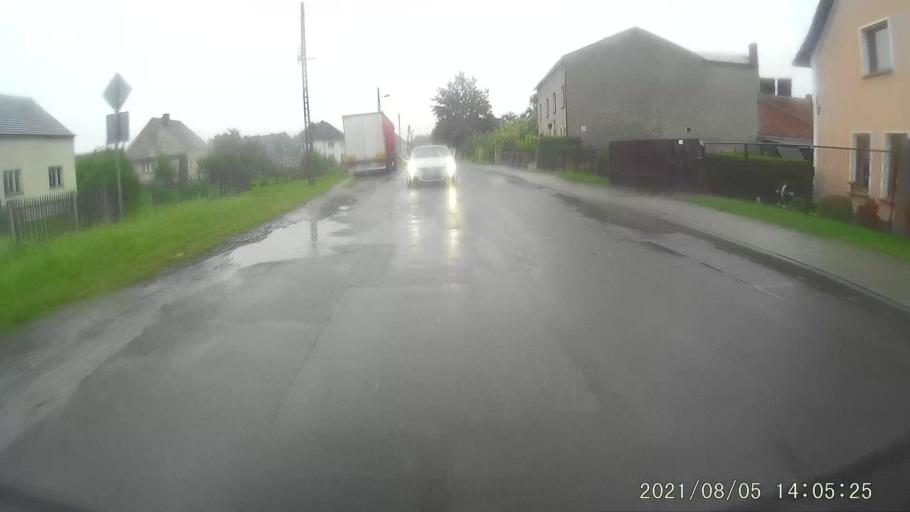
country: PL
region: Opole Voivodeship
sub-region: Powiat krapkowicki
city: Strzeleczki
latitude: 50.4650
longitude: 17.8536
